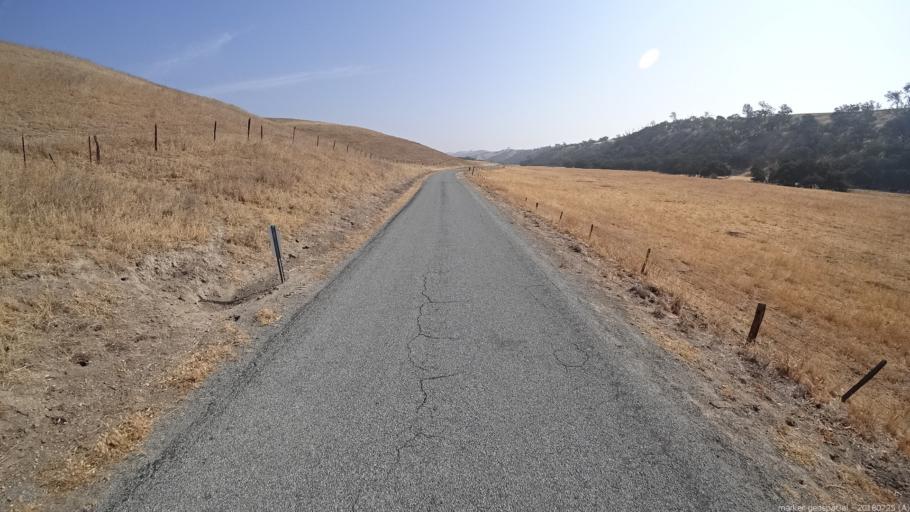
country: US
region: California
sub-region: San Luis Obispo County
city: San Miguel
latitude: 35.8101
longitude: -120.5289
